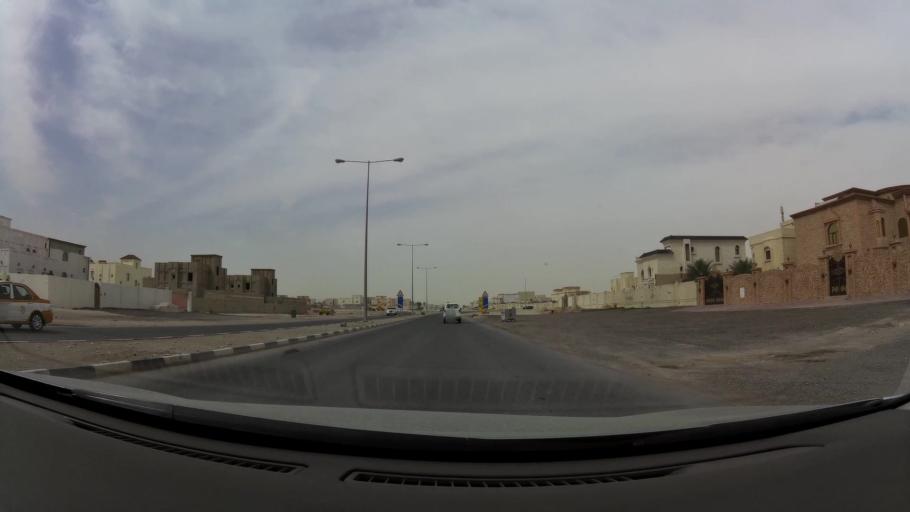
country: QA
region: Baladiyat ad Dawhah
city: Doha
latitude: 25.2093
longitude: 51.4735
